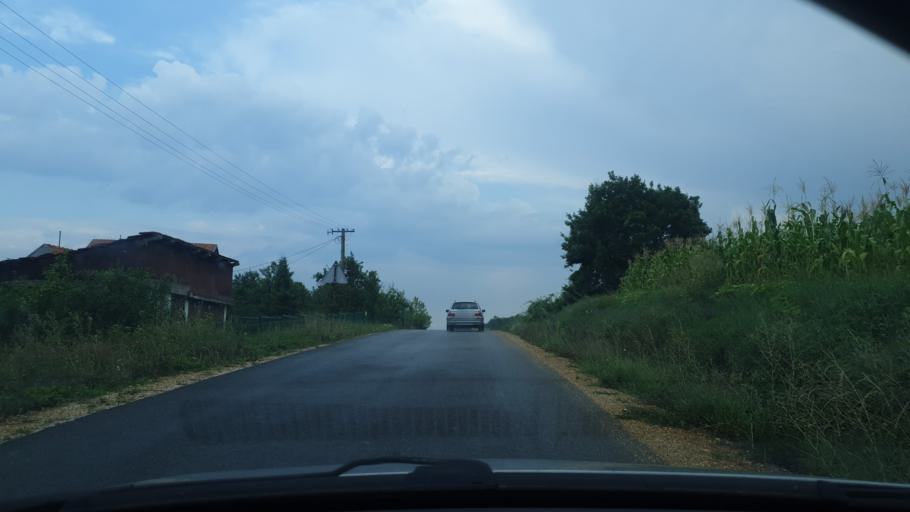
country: RS
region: Central Serbia
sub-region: Sumadijski Okrug
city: Kragujevac
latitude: 44.0592
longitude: 20.7848
